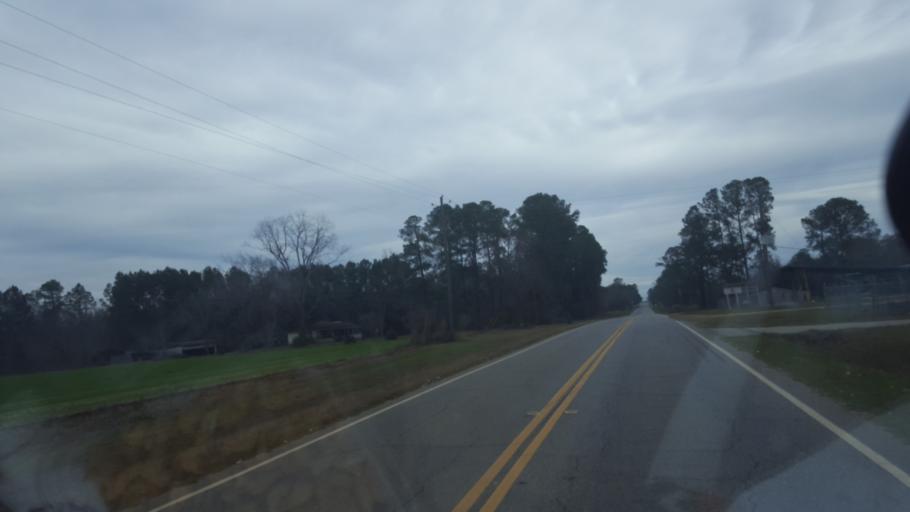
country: US
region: Georgia
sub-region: Wilcox County
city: Rochelle
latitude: 31.7995
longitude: -83.4941
